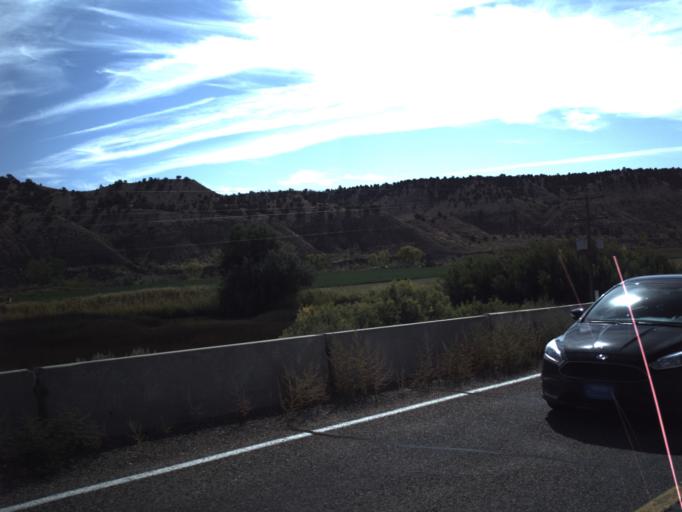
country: US
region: Utah
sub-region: Garfield County
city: Panguitch
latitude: 37.6082
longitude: -112.0607
